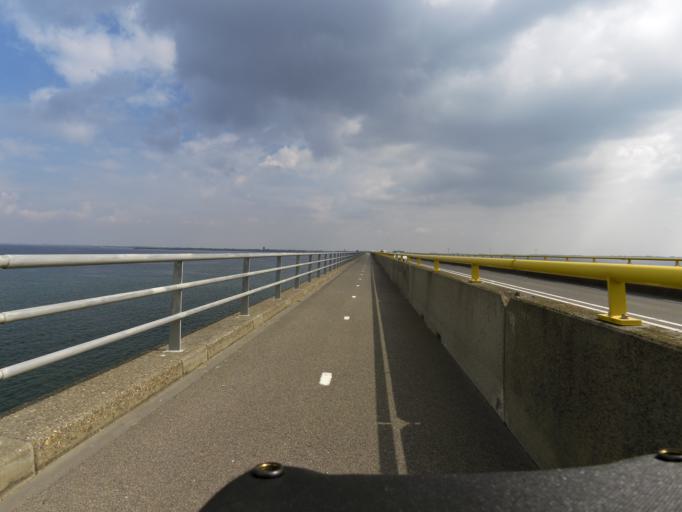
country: NL
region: Zeeland
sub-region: Gemeente Goes
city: Goes
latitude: 51.6097
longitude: 3.8878
